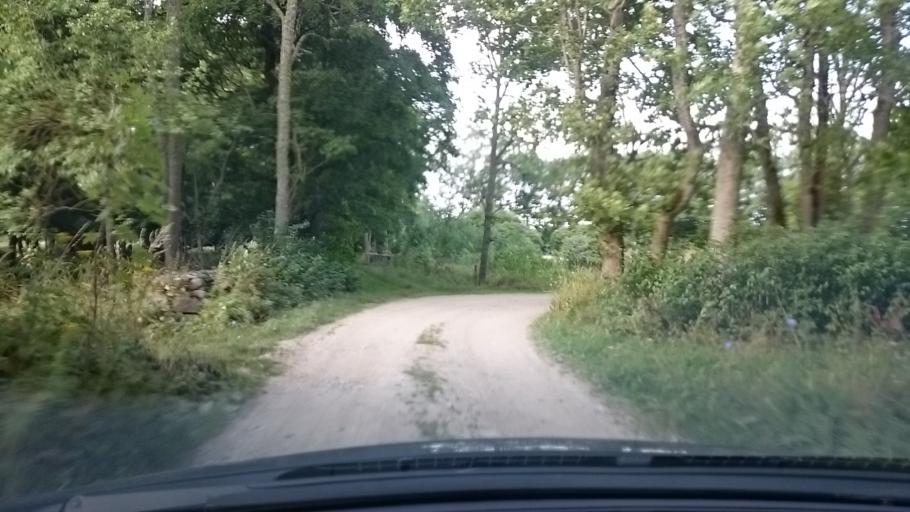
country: EE
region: Saare
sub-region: Kuressaare linn
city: Kuressaare
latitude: 58.3252
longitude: 21.9687
